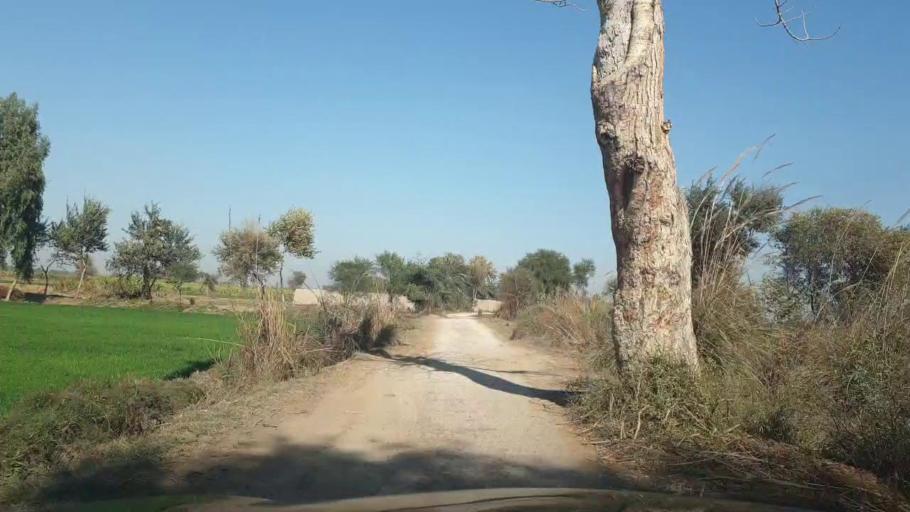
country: PK
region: Sindh
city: Adilpur
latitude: 27.9750
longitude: 69.4185
